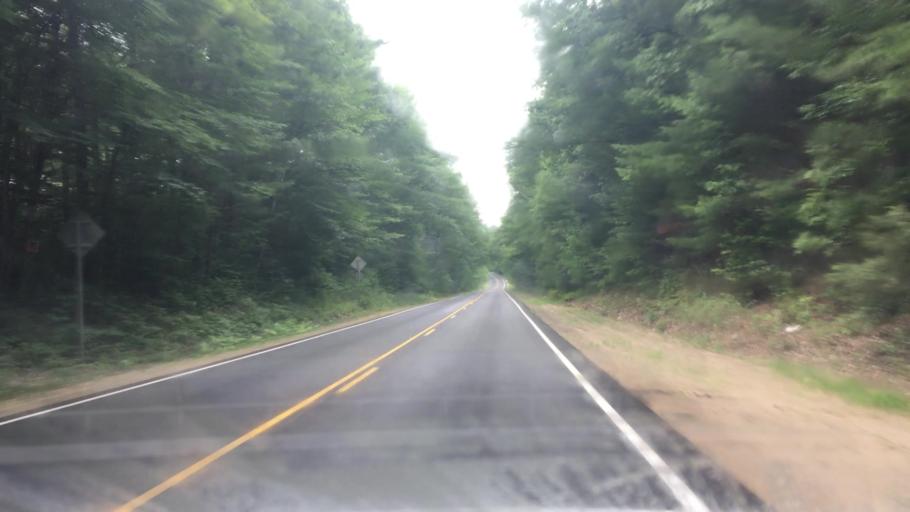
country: US
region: New York
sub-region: Clinton County
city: Morrisonville
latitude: 44.6252
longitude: -73.5923
